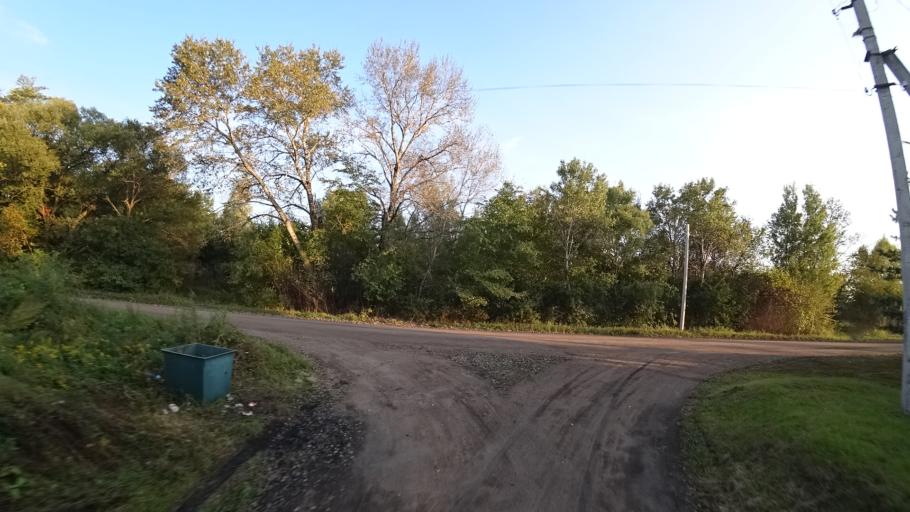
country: RU
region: Amur
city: Arkhara
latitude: 49.3625
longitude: 130.1173
